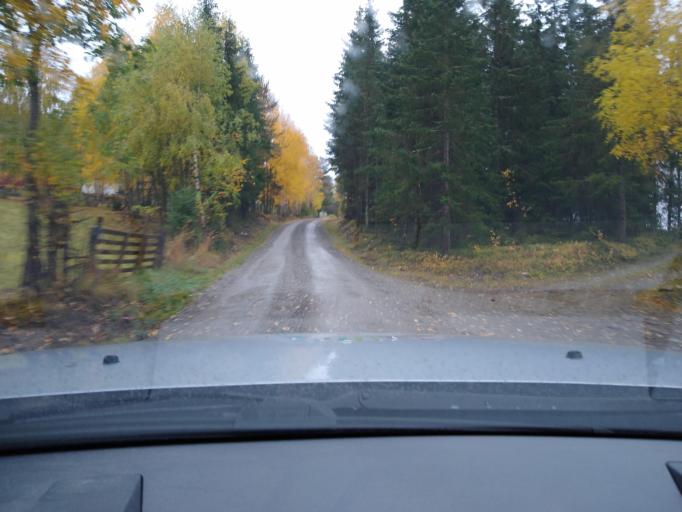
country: NO
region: Oppland
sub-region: Ringebu
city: Ringebu
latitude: 61.5529
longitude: 10.1528
